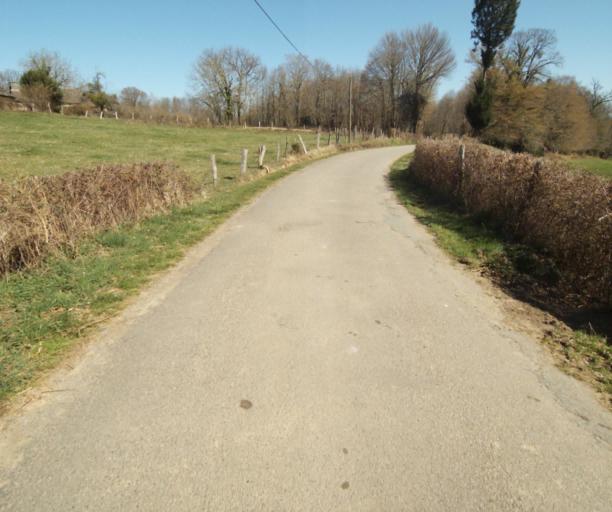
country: FR
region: Limousin
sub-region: Departement de la Correze
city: Saint-Clement
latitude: 45.3038
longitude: 1.7052
